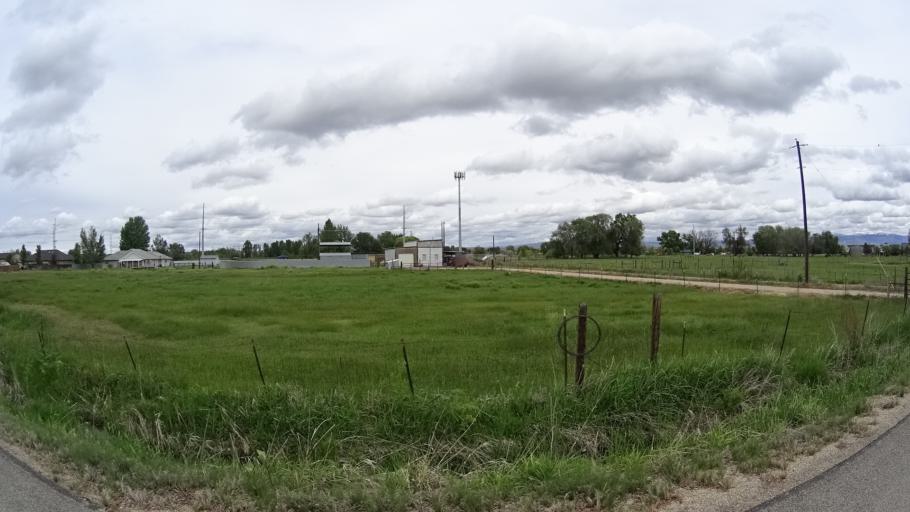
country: US
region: Idaho
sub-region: Ada County
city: Star
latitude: 43.6896
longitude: -116.4560
